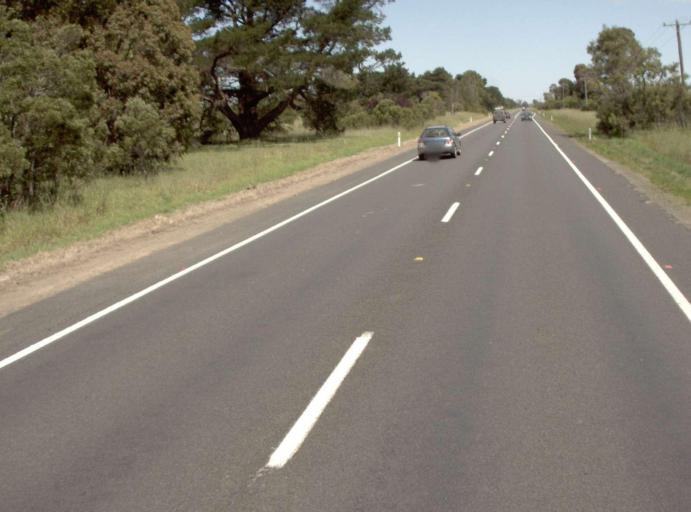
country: AU
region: Victoria
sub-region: Wellington
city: Sale
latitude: -38.0491
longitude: 147.0653
